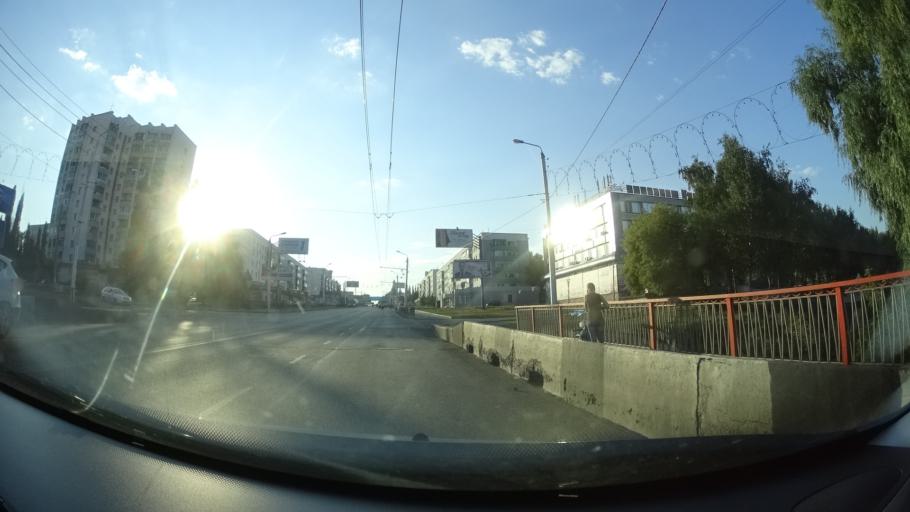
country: RU
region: Bashkortostan
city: Sterlitamak
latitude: 53.6223
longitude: 55.9540
